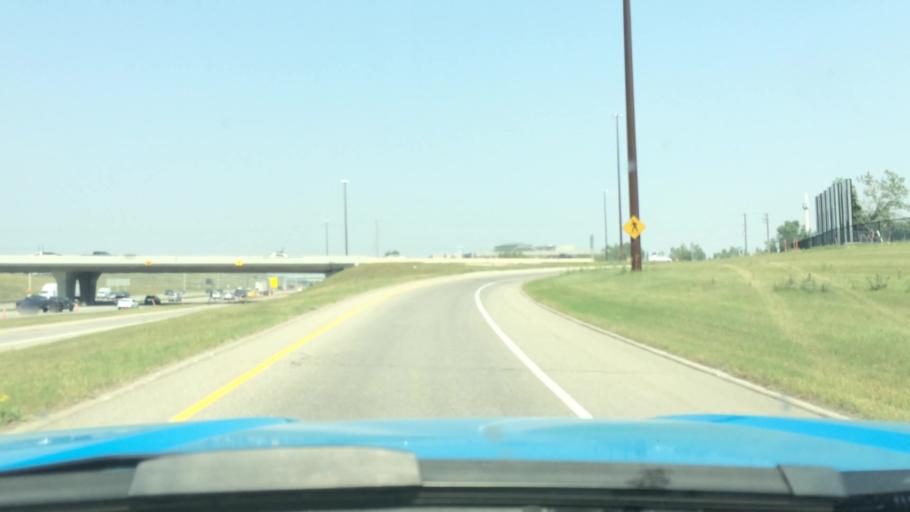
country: CA
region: Alberta
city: Calgary
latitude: 51.1093
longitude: -114.0464
